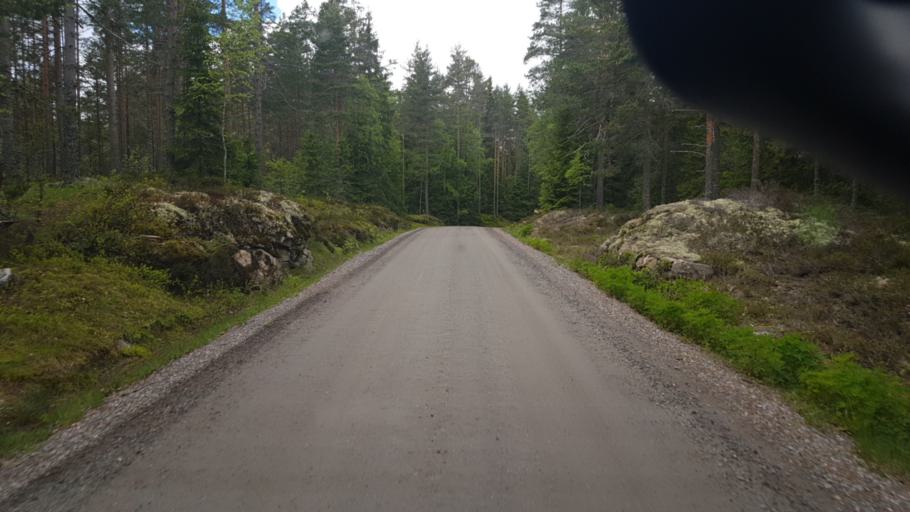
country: NO
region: Ostfold
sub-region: Romskog
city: Romskog
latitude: 59.7120
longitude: 12.0127
